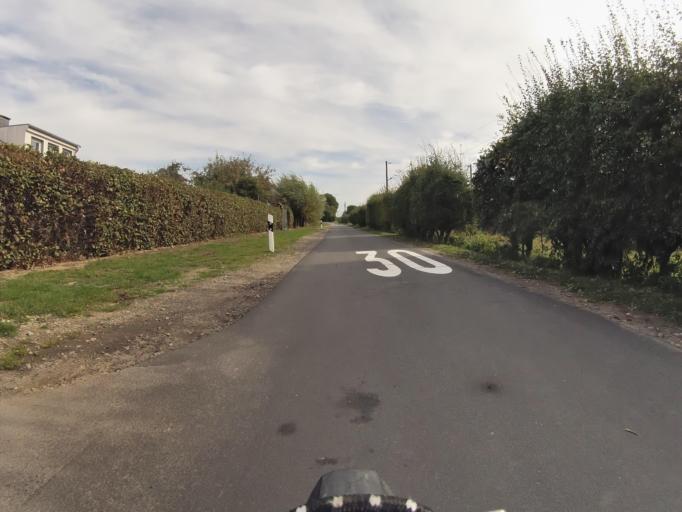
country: DE
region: North Rhine-Westphalia
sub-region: Regierungsbezirk Munster
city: Mettingen
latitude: 52.2672
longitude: 7.7728
